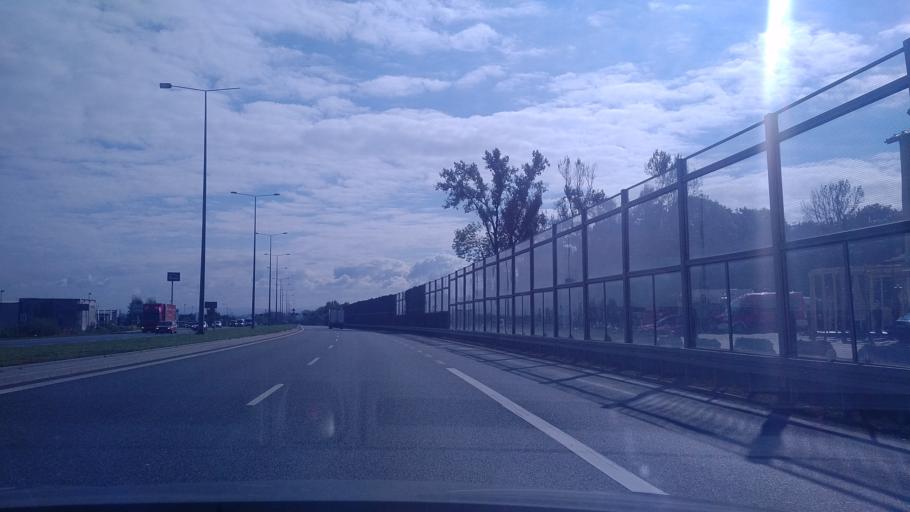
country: PL
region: Lesser Poland Voivodeship
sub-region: Powiat krakowski
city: Modlniczka
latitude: 50.1154
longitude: 19.8700
